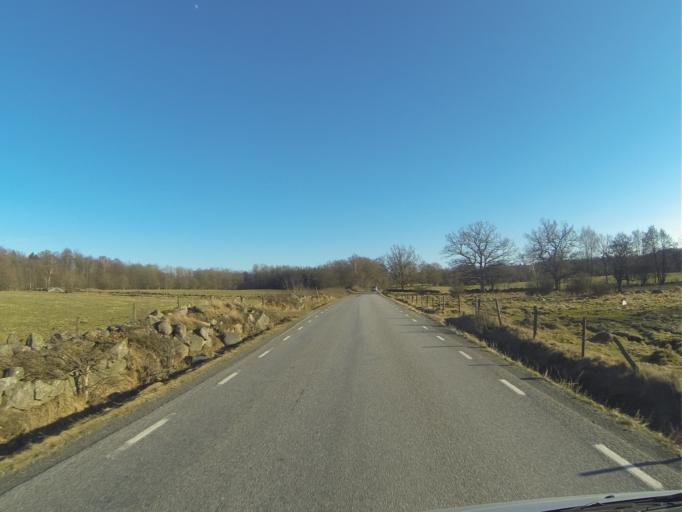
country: SE
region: Skane
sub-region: Horby Kommun
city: Hoerby
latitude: 55.8941
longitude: 13.6650
